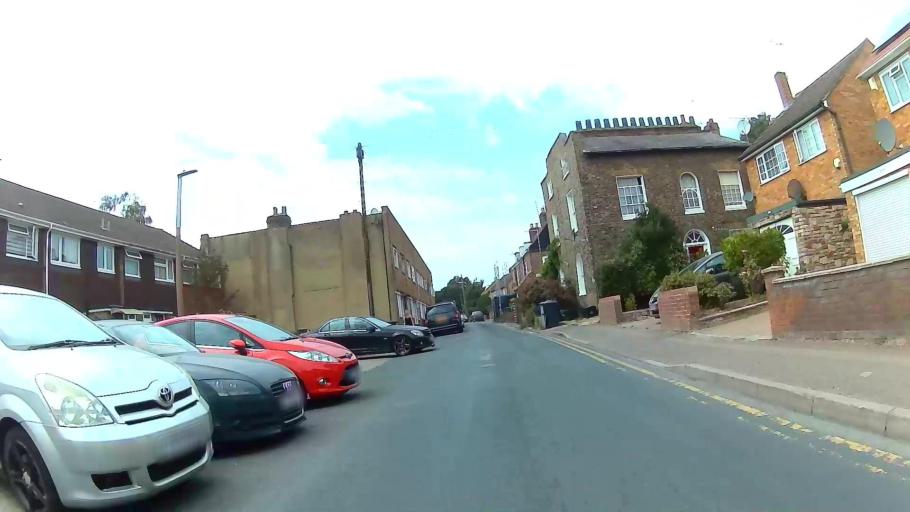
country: GB
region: England
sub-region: Hertfordshire
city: Waltham Cross
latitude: 51.6868
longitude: -0.0350
